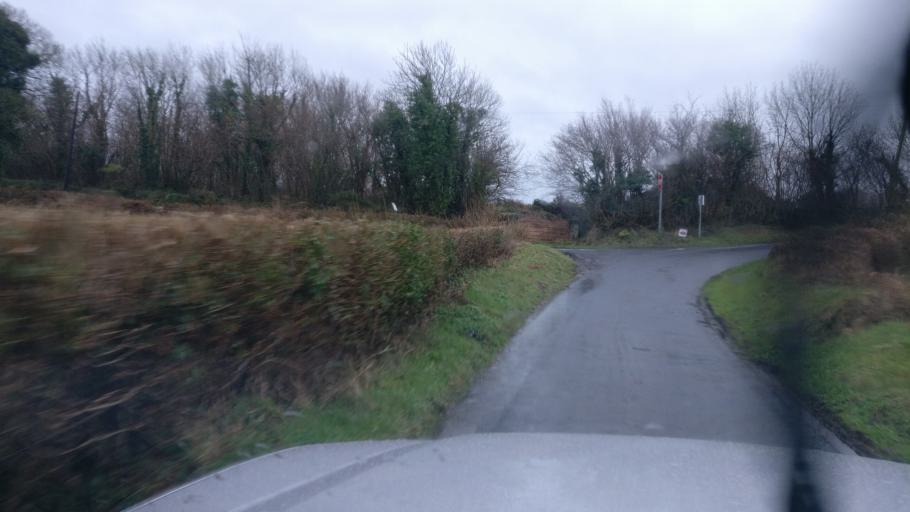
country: IE
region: Connaught
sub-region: County Galway
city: Ballinasloe
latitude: 53.2926
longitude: -8.2749
